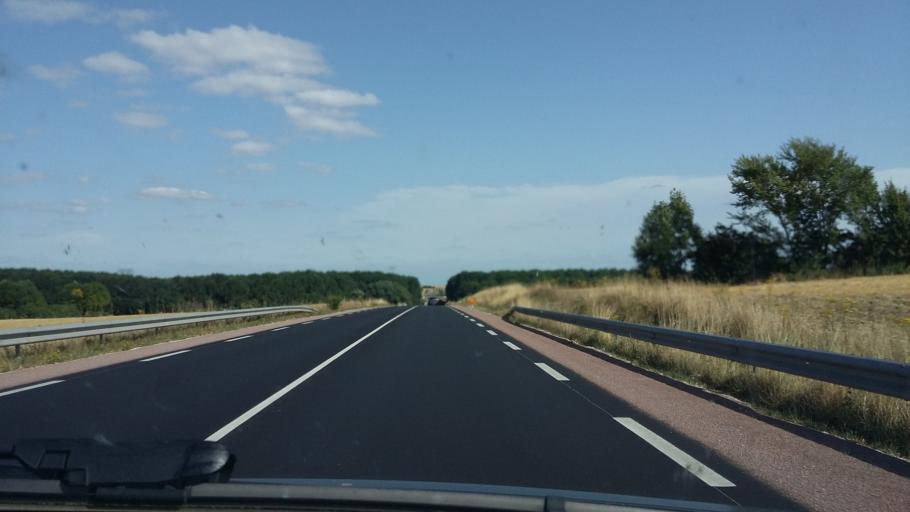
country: FR
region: Poitou-Charentes
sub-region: Departement de la Charente-Maritime
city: Saint-Jean-d'Angely
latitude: 45.9451
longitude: -0.4951
